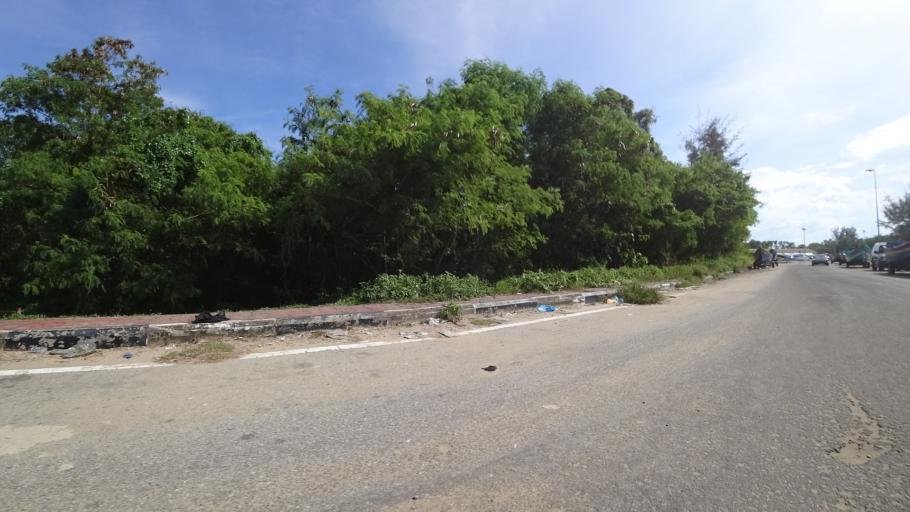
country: BN
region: Brunei and Muara
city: Bandar Seri Begawan
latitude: 4.9574
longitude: 114.8406
